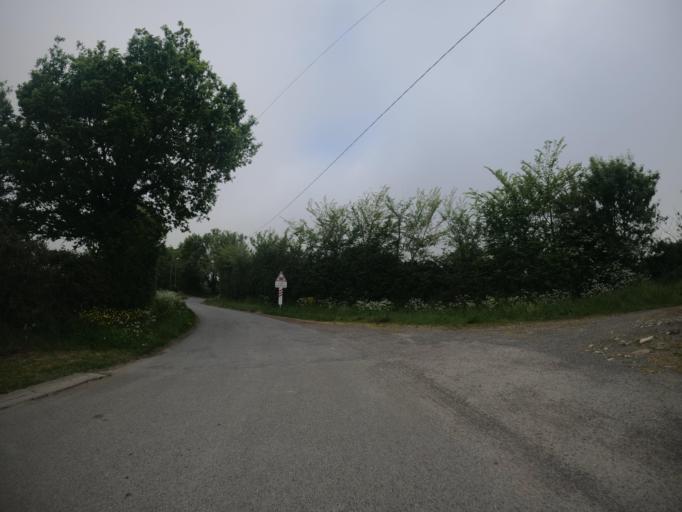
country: FR
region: Poitou-Charentes
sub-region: Departement des Deux-Sevres
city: Mauze-Thouarsais
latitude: 46.8979
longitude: -0.3315
